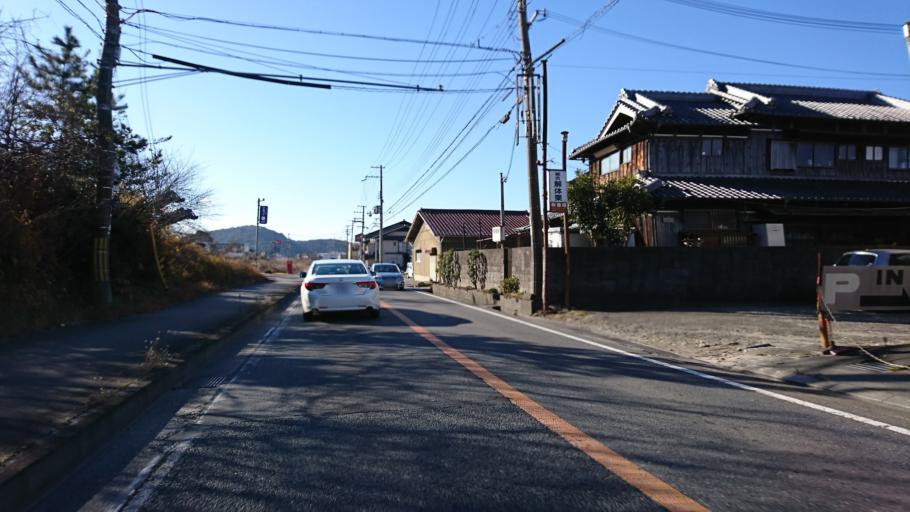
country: JP
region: Hyogo
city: Kakogawacho-honmachi
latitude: 34.8112
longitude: 134.8364
